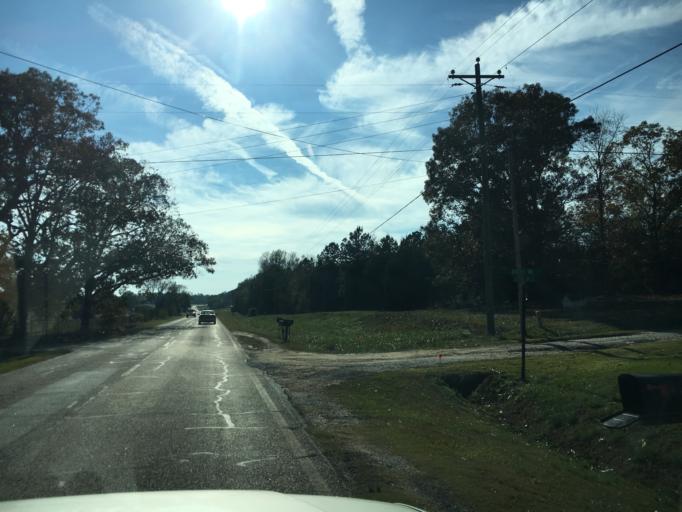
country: US
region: Georgia
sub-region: Hart County
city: Hartwell
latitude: 34.2961
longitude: -82.8393
